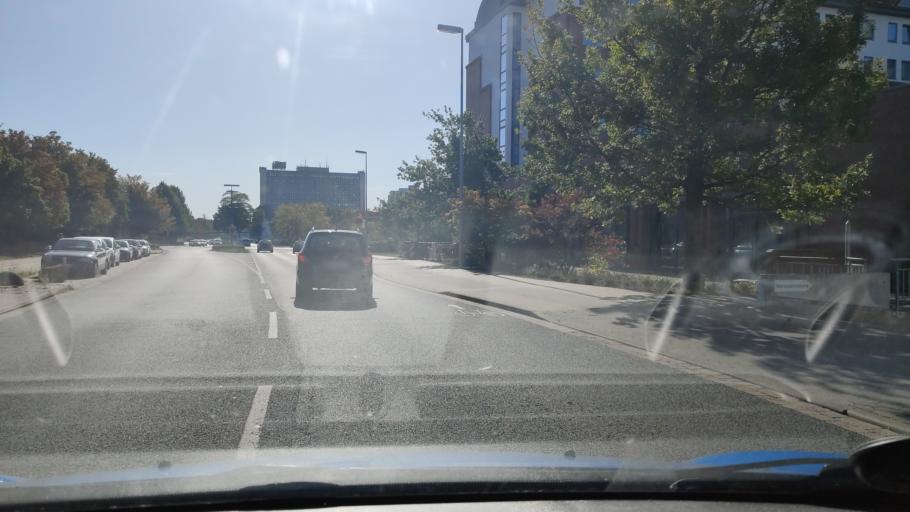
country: DE
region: Lower Saxony
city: Laatzen
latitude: 52.3108
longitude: 9.8091
